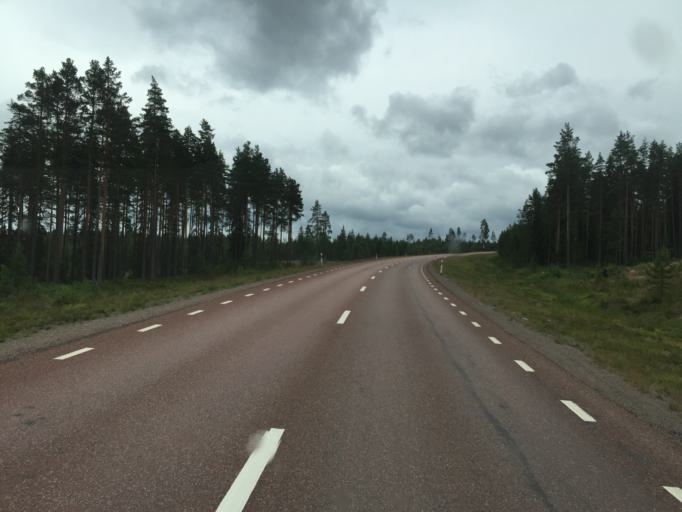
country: SE
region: Dalarna
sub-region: Malung-Saelens kommun
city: Malung
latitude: 60.6670
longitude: 13.7011
